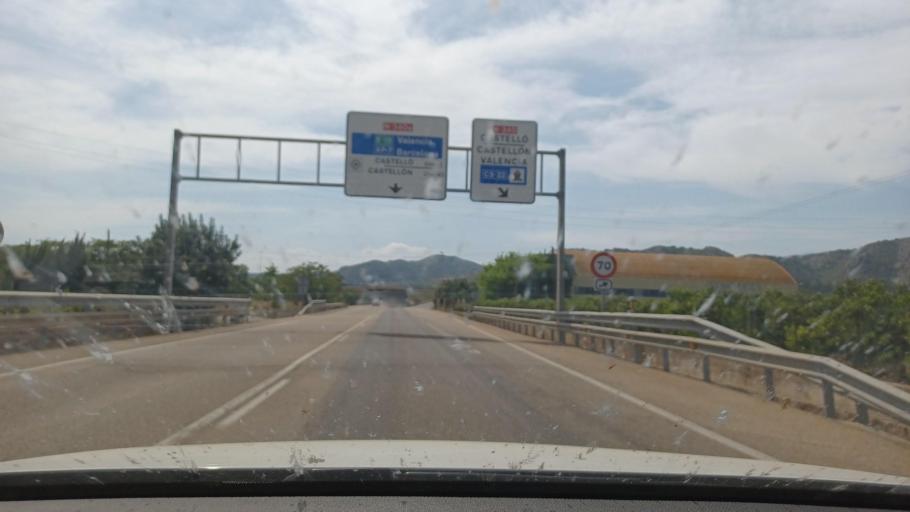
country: ES
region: Valencia
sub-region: Provincia de Castello
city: Castello de la Plana
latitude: 40.0252
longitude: -0.0143
